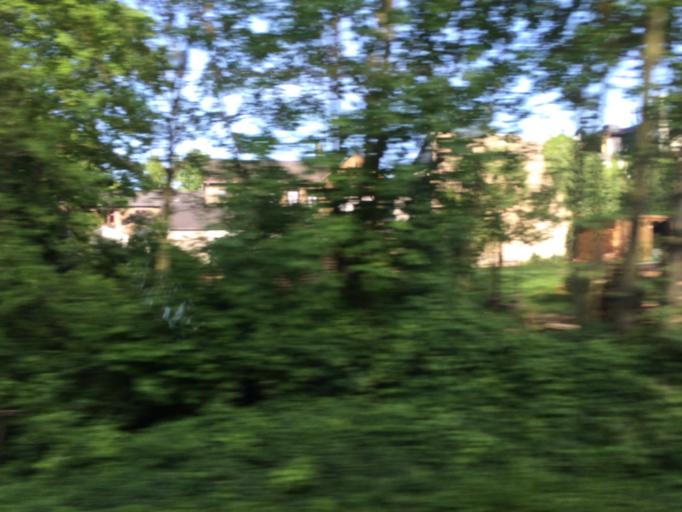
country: DE
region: Rheinland-Pfalz
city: Koblenz
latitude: 50.3287
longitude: 7.5949
